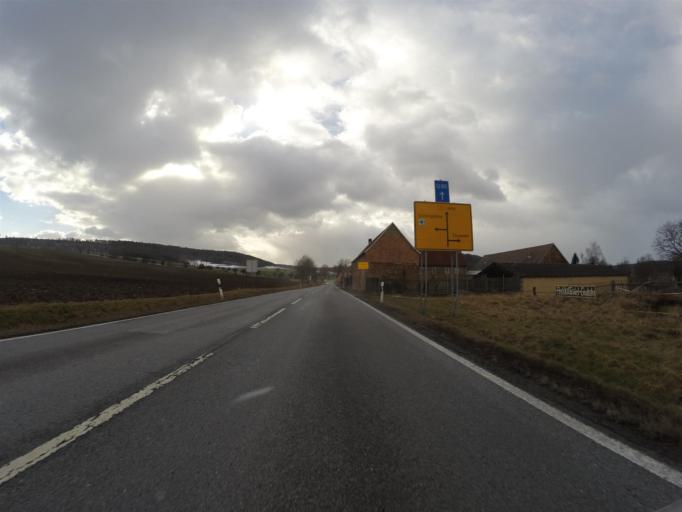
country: DE
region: Thuringia
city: Nausnitz
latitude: 50.9355
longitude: 11.7206
